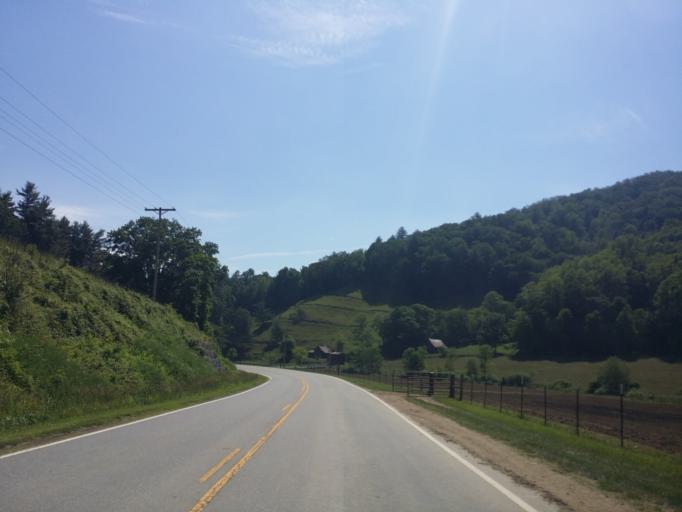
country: US
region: North Carolina
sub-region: Madison County
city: Marshall
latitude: 35.7006
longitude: -82.8045
